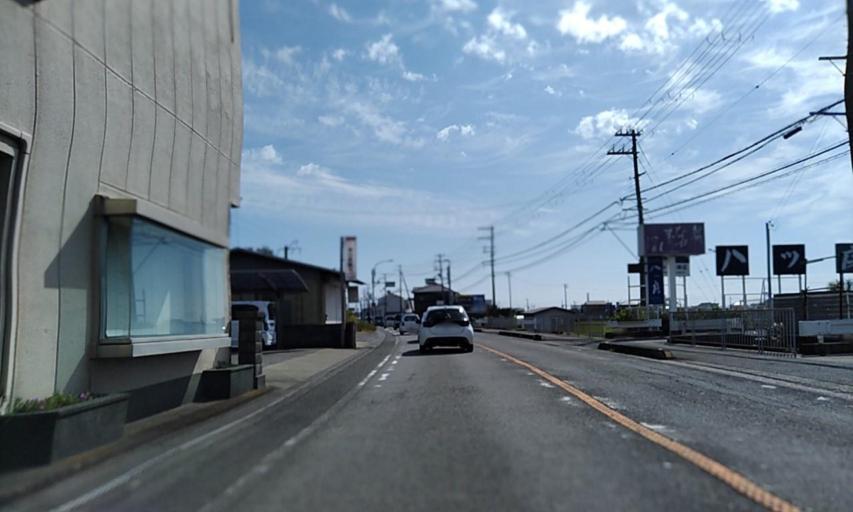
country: JP
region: Wakayama
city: Gobo
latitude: 33.9108
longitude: 135.1496
